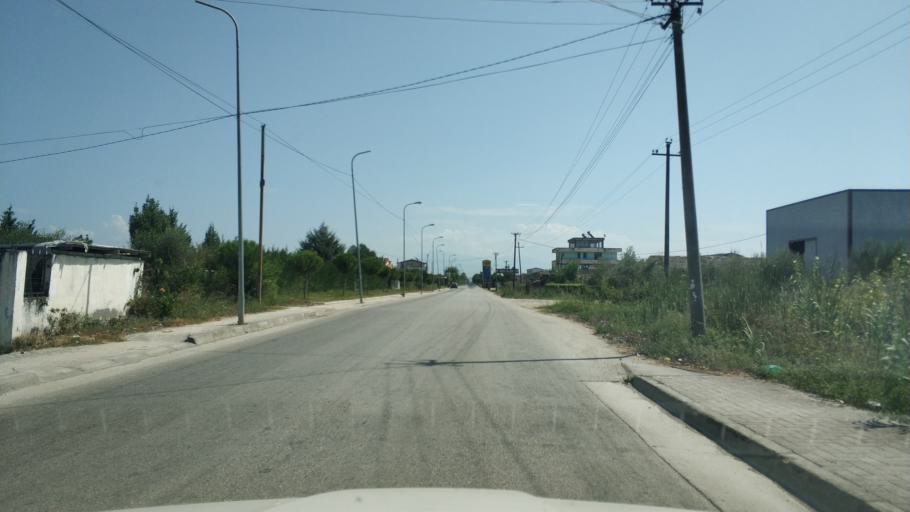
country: AL
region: Fier
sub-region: Rrethi i Lushnjes
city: Krutja e Poshtme
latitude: 40.8917
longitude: 19.6378
